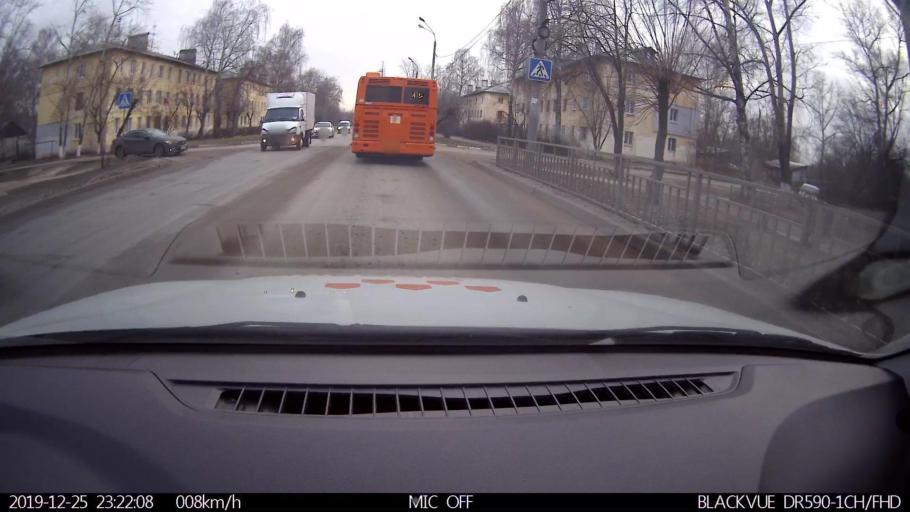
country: RU
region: Nizjnij Novgorod
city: Gorbatovka
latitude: 56.3526
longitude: 43.8337
